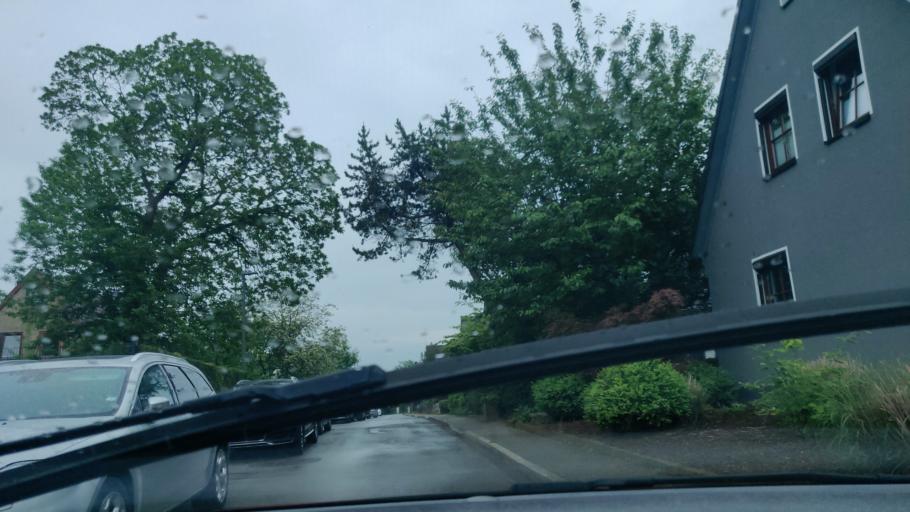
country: DE
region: North Rhine-Westphalia
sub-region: Regierungsbezirk Dusseldorf
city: Heiligenhaus
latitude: 51.3336
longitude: 6.9557
